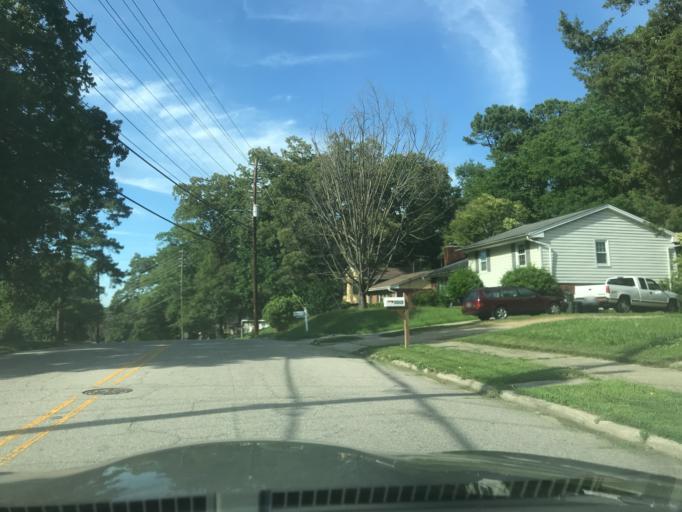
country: US
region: North Carolina
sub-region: Wake County
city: Raleigh
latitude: 35.8294
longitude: -78.6006
